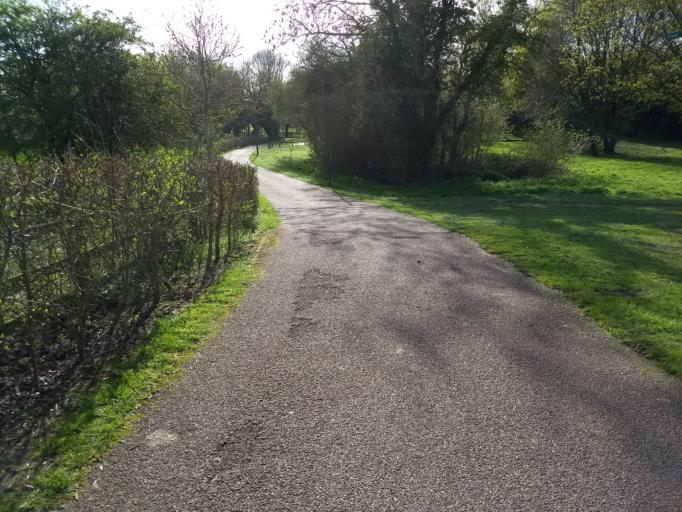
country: GB
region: England
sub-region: Milton Keynes
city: Simpson
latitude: 52.0242
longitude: -0.7189
